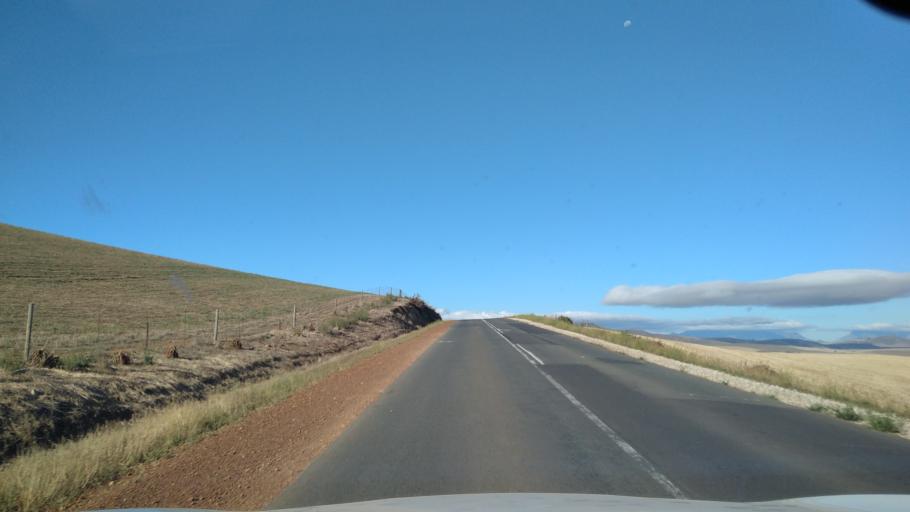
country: ZA
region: Western Cape
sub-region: Overberg District Municipality
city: Caledon
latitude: -34.1835
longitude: 19.2749
